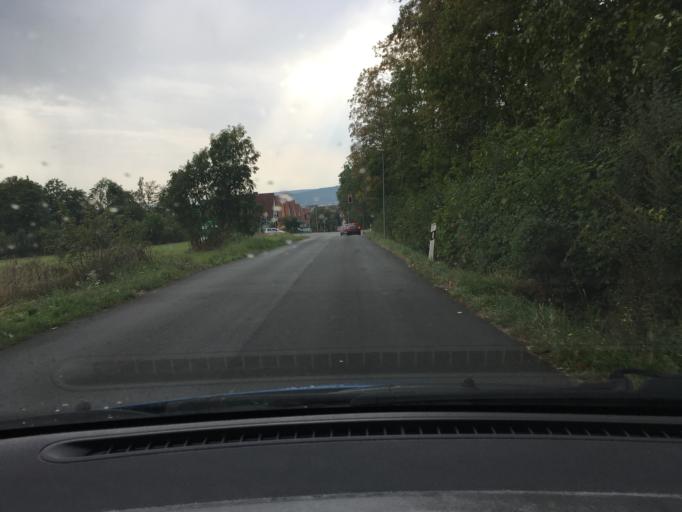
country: DE
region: Lower Saxony
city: Bad Munder am Deister
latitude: 52.2046
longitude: 9.4719
